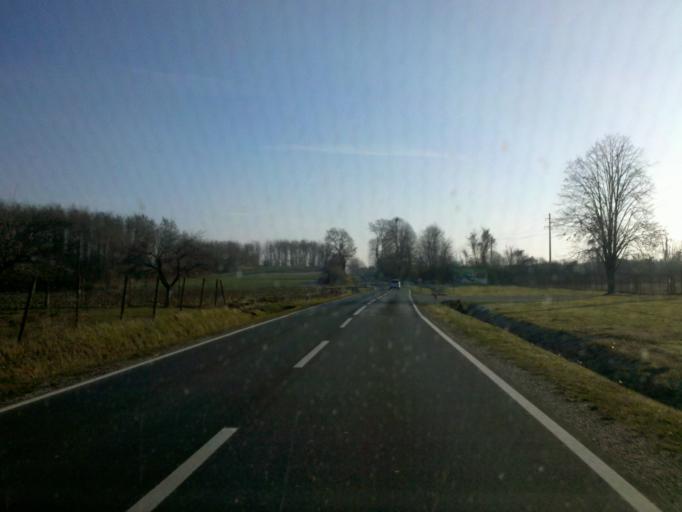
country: HR
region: Koprivnicko-Krizevacka
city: Peteranec
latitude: 46.1121
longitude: 16.8931
